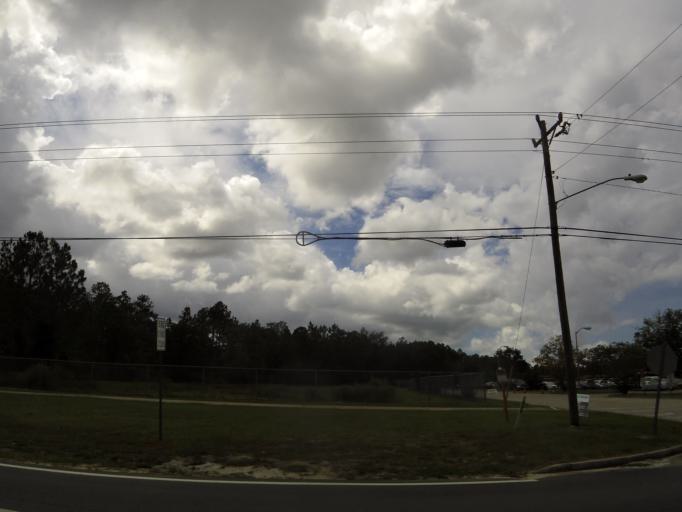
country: US
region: Florida
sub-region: Clay County
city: Middleburg
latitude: 30.0810
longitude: -81.9391
